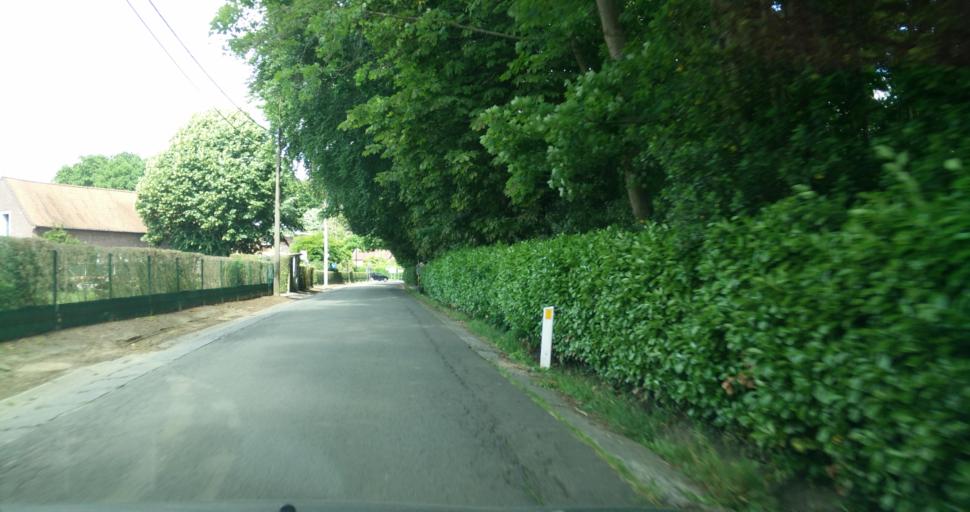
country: BE
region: Flanders
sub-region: Provincie Oost-Vlaanderen
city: Ronse
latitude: 50.7699
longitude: 3.6328
